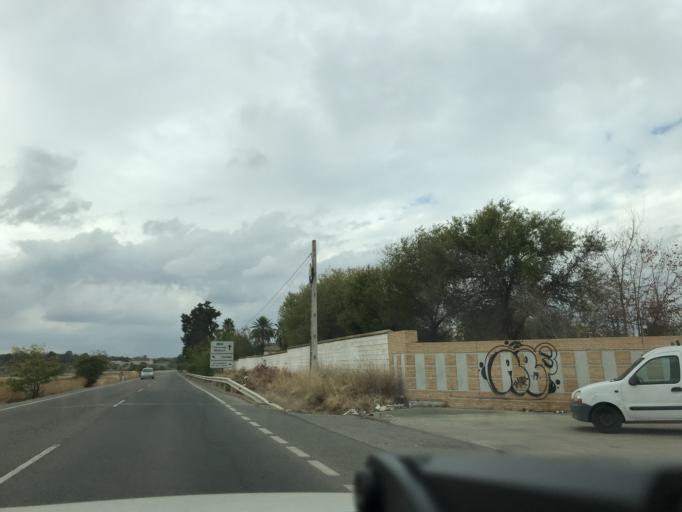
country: ES
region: Andalusia
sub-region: Provincia de Sevilla
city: Villanueva del Rio y Minas
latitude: 37.6377
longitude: -5.7332
